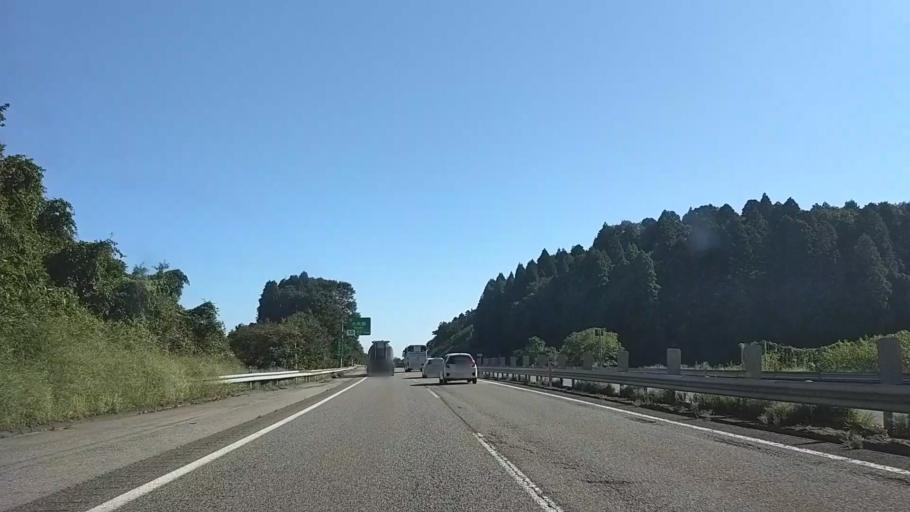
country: JP
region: Toyama
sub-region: Oyabe Shi
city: Oyabe
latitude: 36.6254
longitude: 136.8347
